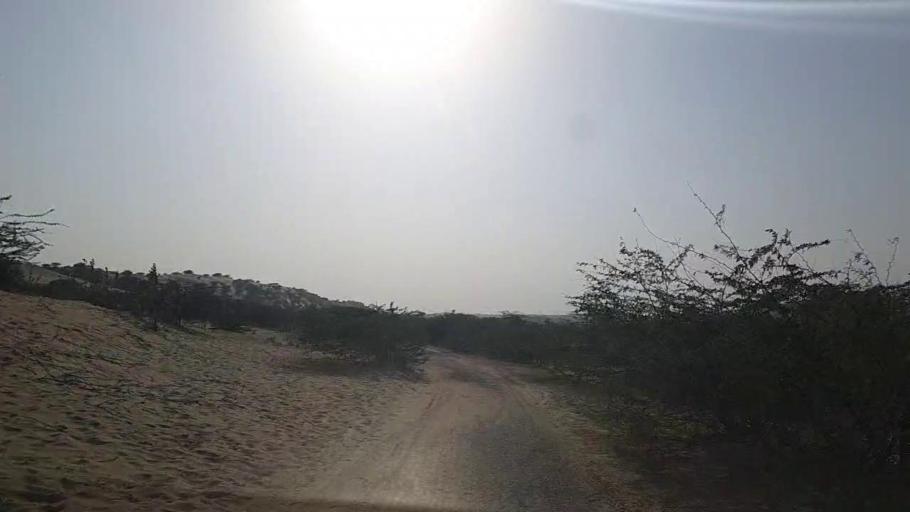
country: PK
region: Sindh
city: Naukot
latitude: 24.6178
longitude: 69.3708
